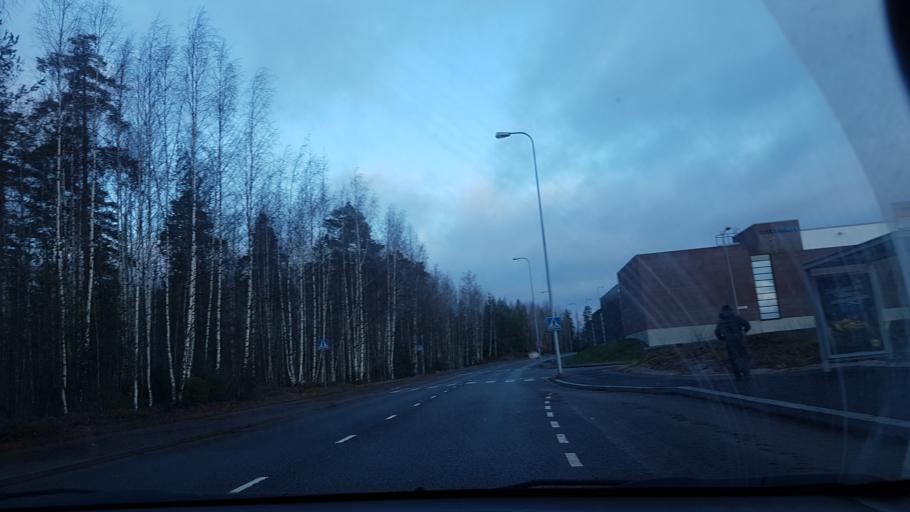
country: FI
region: Uusimaa
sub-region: Helsinki
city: Kilo
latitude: 60.3081
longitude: 24.8513
